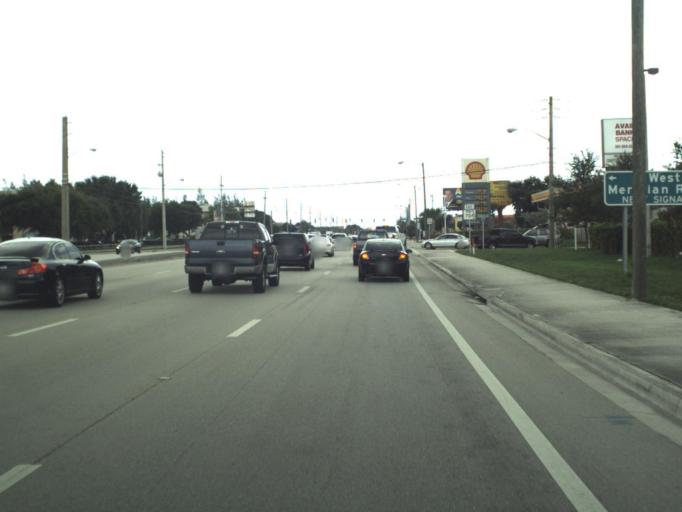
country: US
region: Florida
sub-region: Palm Beach County
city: Plantation Mobile Home Park
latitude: 26.7073
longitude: -80.1366
